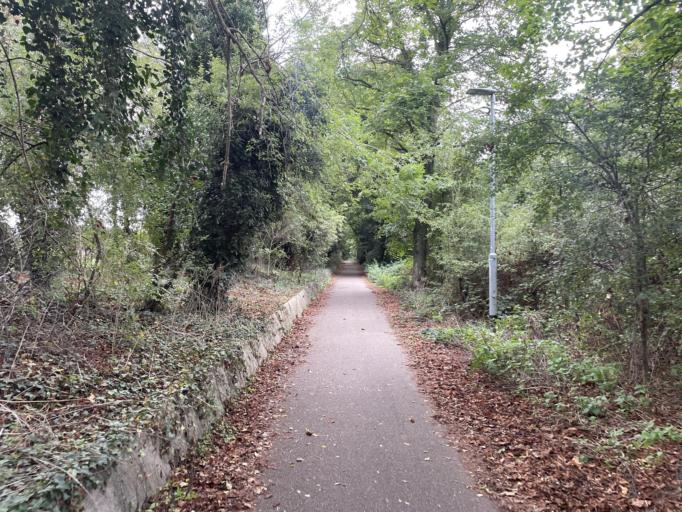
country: GB
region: England
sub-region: Hertfordshire
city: Hatfield
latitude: 51.7756
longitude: -0.2222
